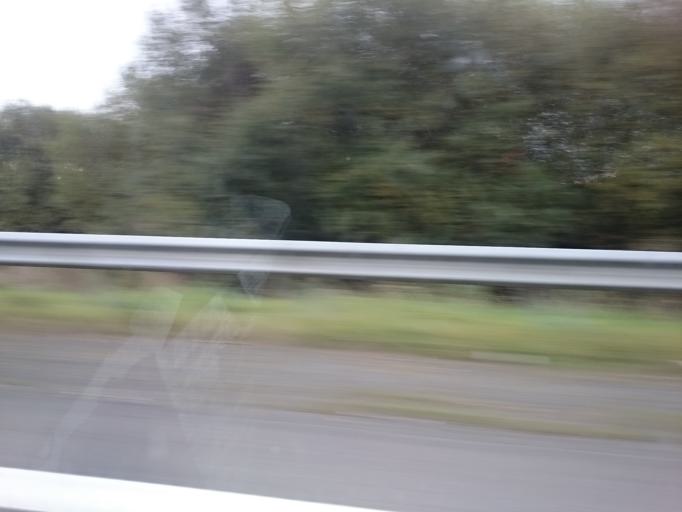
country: FR
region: Brittany
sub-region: Departement d'Ille-et-Vilaine
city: Quedillac
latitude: 48.2226
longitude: -2.1121
